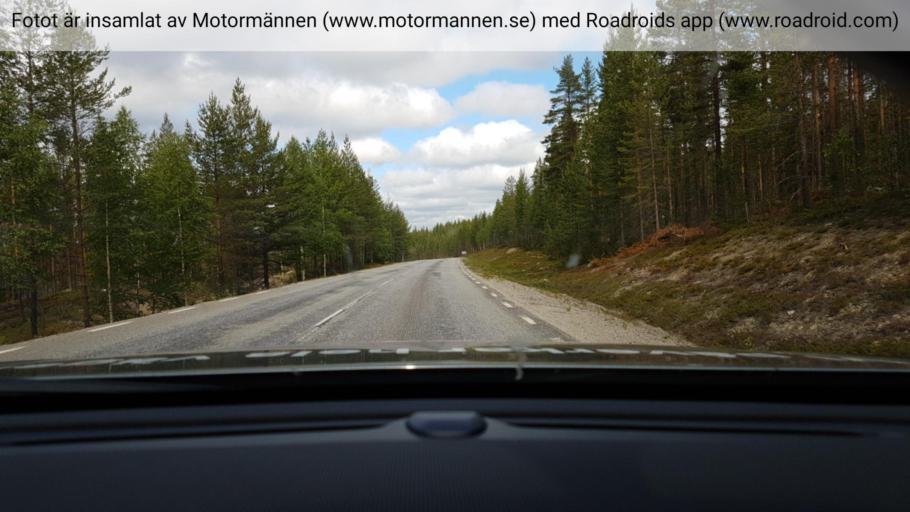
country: SE
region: Vaesterbotten
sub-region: Lycksele Kommun
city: Lycksele
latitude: 64.8539
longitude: 18.7456
